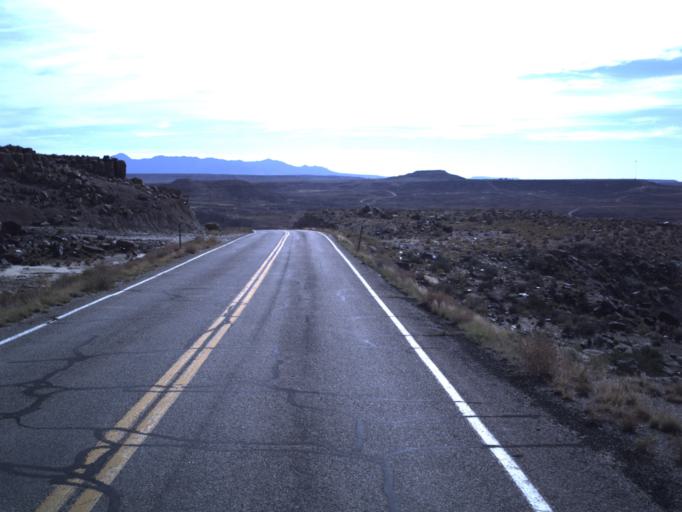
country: US
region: Utah
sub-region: San Juan County
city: Blanding
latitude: 37.3220
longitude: -109.3189
